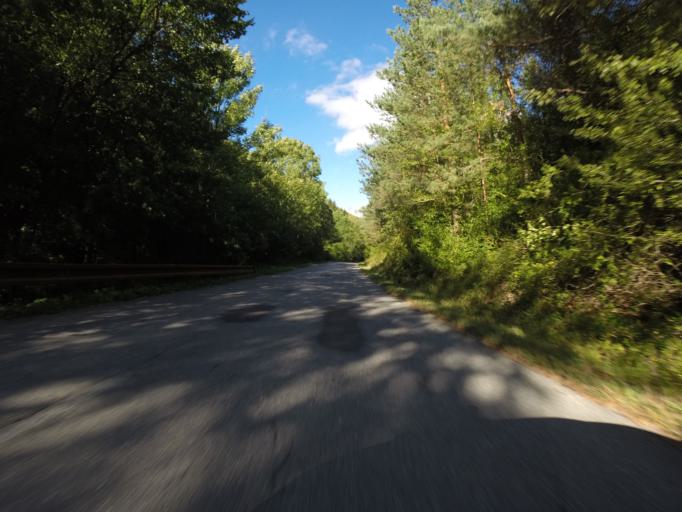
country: SK
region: Trenciansky
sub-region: Okres Povazska Bystrica
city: Povazska Bystrica
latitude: 48.9669
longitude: 18.4006
